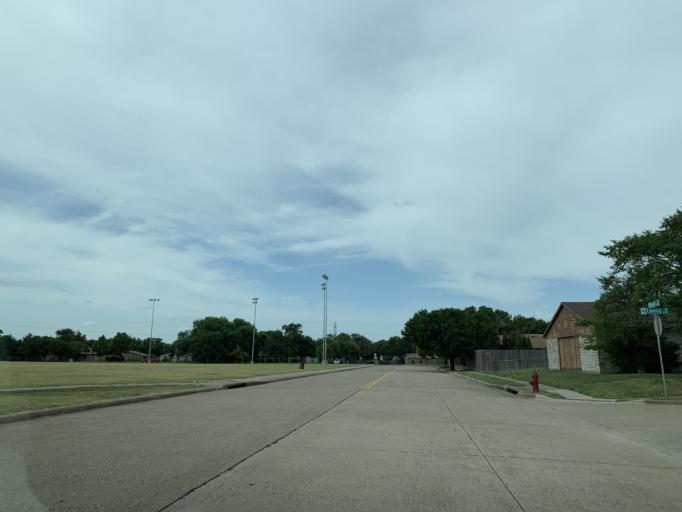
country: US
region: Texas
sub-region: Dallas County
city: Cedar Hill
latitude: 32.6541
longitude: -97.0209
